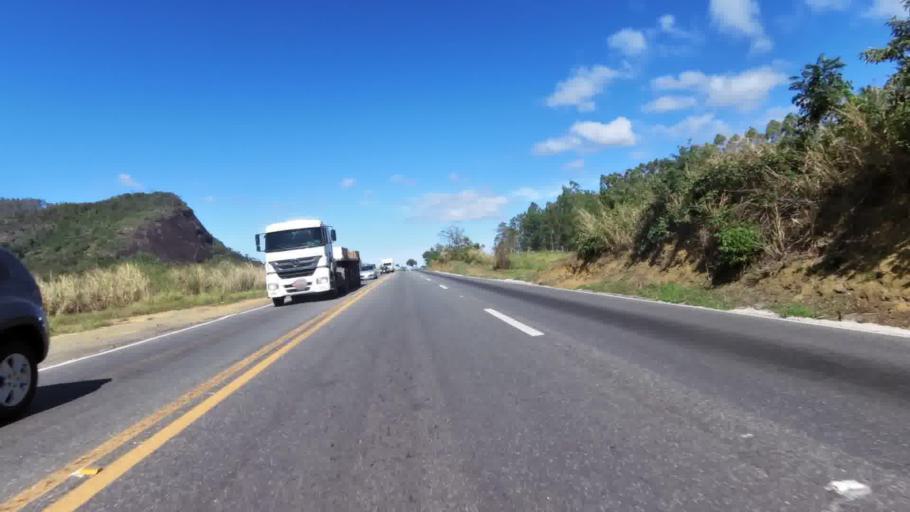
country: BR
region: Espirito Santo
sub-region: Alfredo Chaves
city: Alfredo Chaves
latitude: -20.6934
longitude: -40.7060
